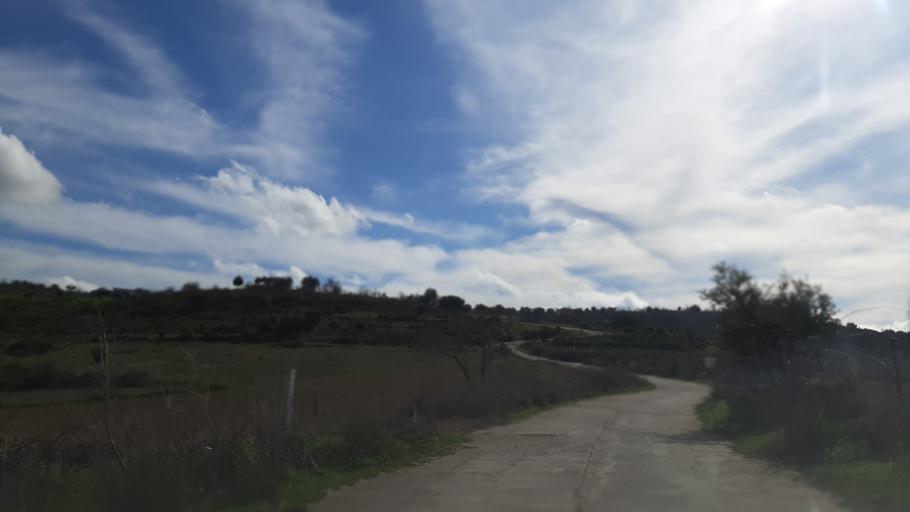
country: ES
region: Castille and Leon
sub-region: Provincia de Salamanca
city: Villarino de los Aires
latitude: 41.2567
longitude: -6.5267
